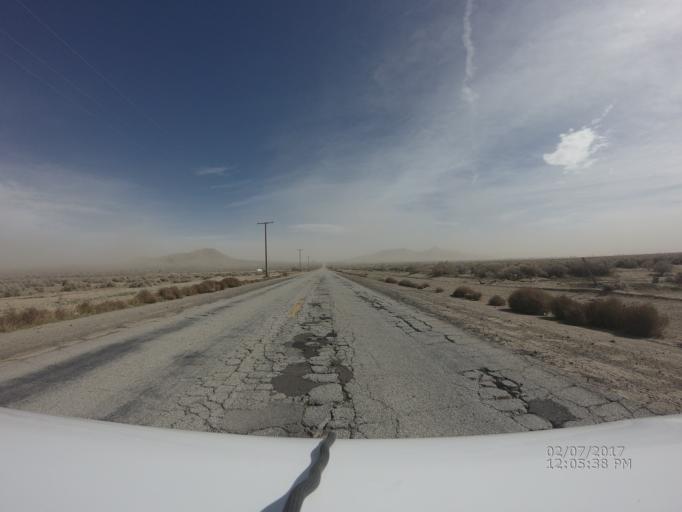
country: US
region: California
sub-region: Los Angeles County
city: Lake Los Angeles
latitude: 34.6901
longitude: -117.8563
